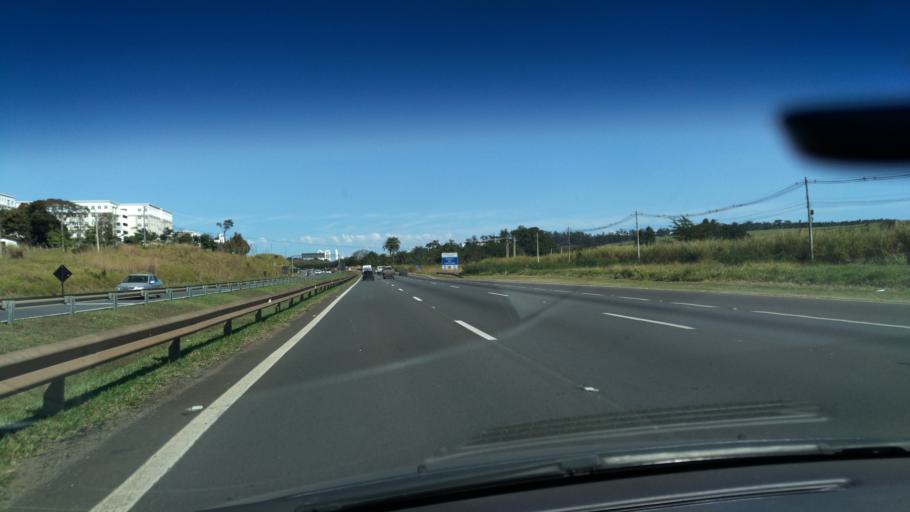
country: BR
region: Sao Paulo
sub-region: Campinas
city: Campinas
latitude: -22.8160
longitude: -47.0361
